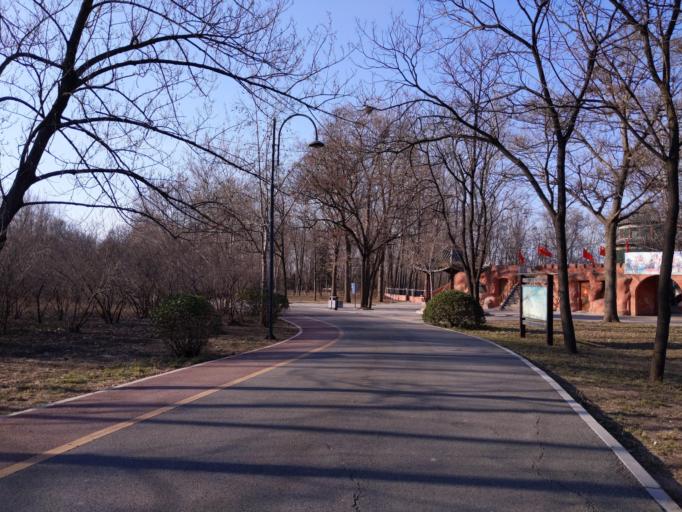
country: CN
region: Henan Sheng
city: Puyang
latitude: 35.7781
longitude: 114.9641
